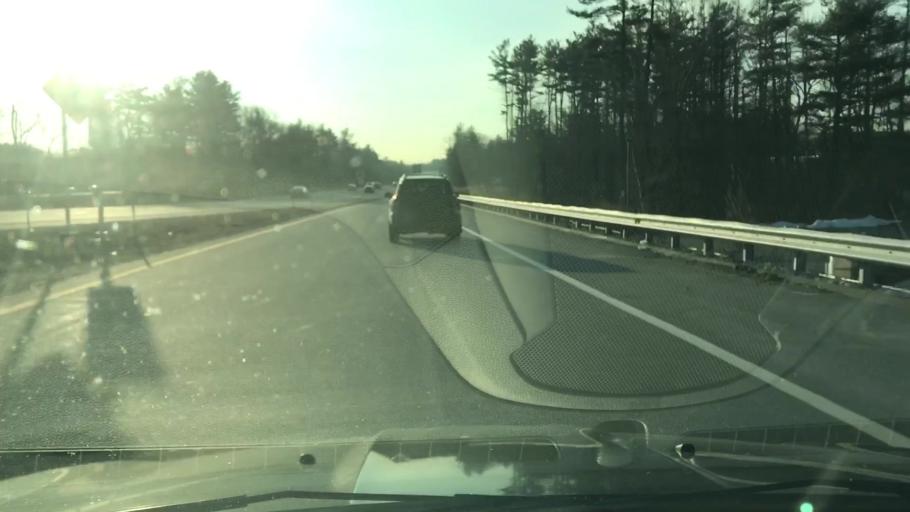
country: US
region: New Hampshire
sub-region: Rockingham County
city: Salem
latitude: 42.7746
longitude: -71.2437
